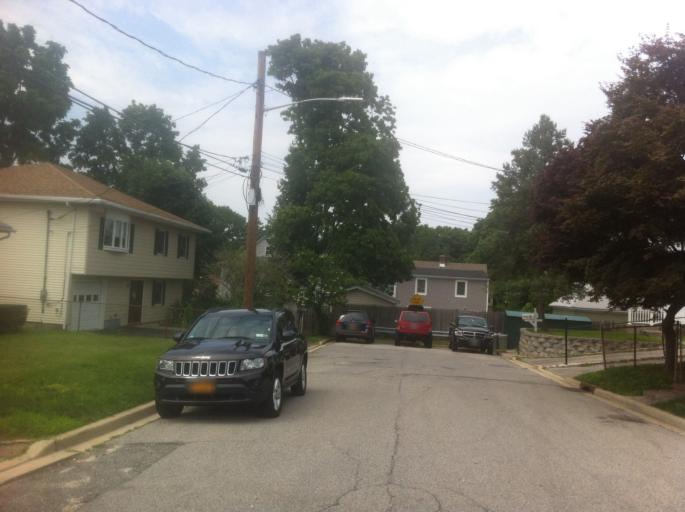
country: US
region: New York
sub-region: Nassau County
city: Locust Valley
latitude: 40.8758
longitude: -73.6108
